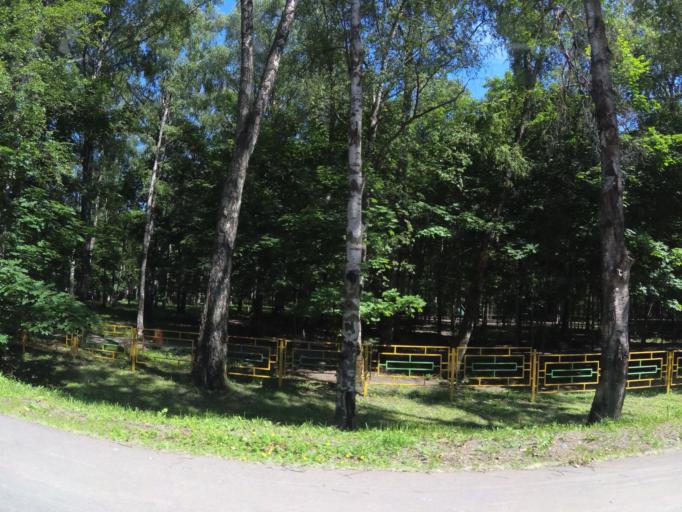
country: RU
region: Moskovskaya
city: Lobnya
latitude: 56.0124
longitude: 37.4682
